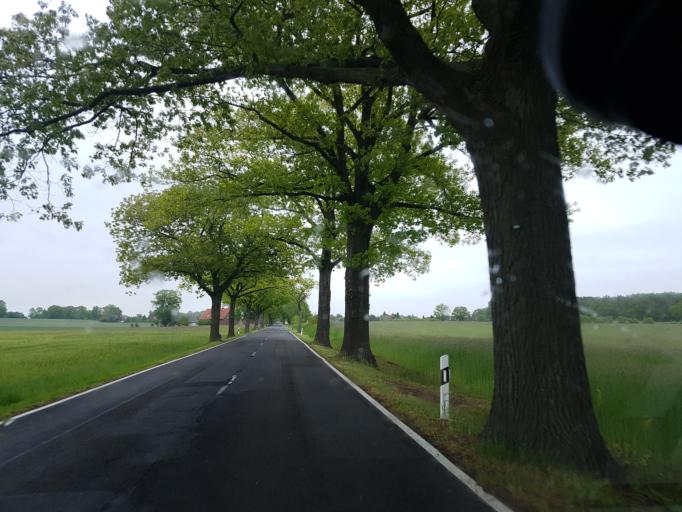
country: DE
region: Brandenburg
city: Cottbus
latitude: 51.6719
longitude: 14.3507
